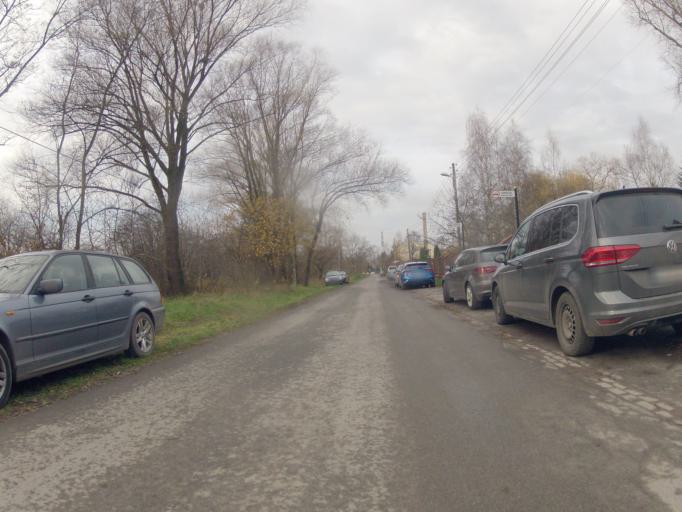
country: PL
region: Lesser Poland Voivodeship
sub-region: Powiat krakowski
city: Rzaska
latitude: 50.0807
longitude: 19.8519
